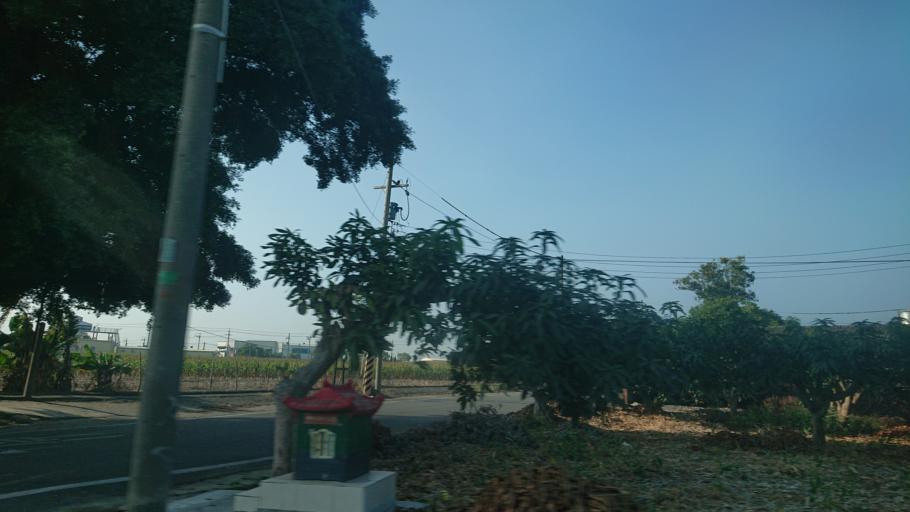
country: TW
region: Taiwan
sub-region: Tainan
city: Tainan
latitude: 23.1260
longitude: 120.2265
